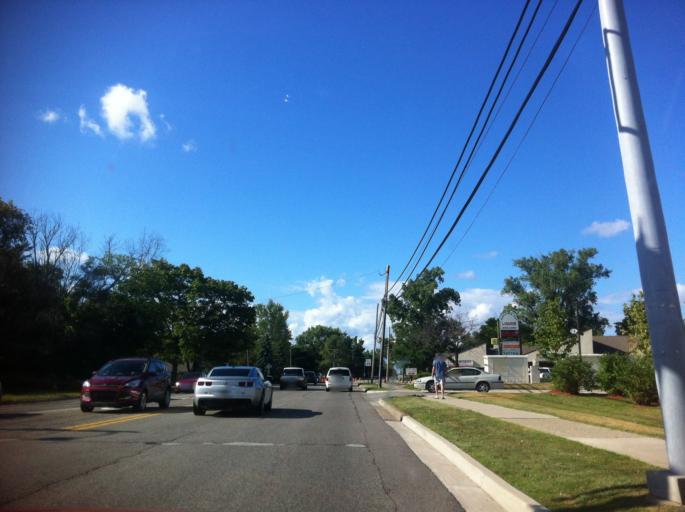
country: US
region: Michigan
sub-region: Washtenaw County
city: Ann Arbor
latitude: 42.2947
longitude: -83.7808
